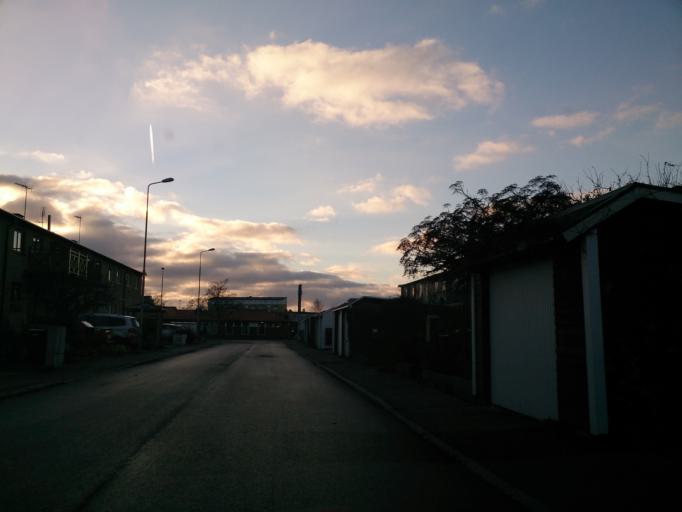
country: SE
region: OEstergoetland
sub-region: Norrkopings Kommun
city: Norrkoping
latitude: 58.6074
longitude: 16.1489
